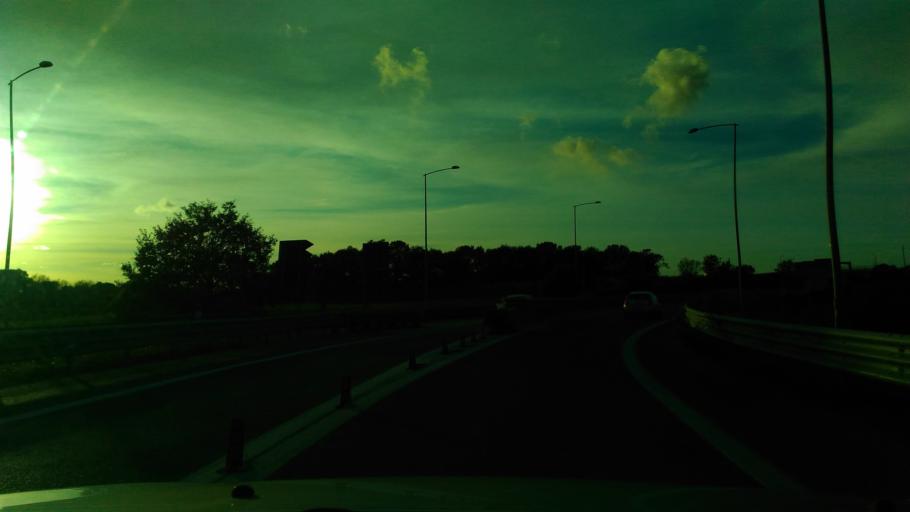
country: IT
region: Tuscany
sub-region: Provincia di Livorno
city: Rosignano Marittimo
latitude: 43.3724
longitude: 10.4995
